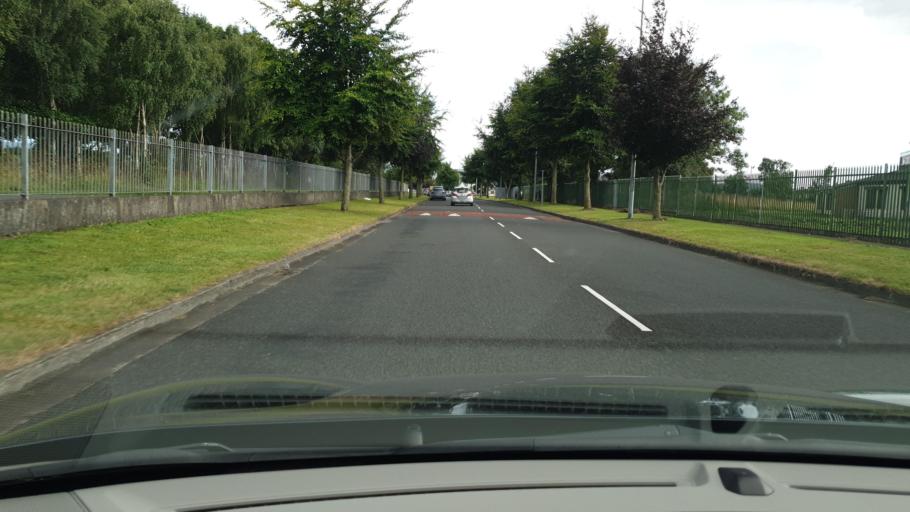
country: IE
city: Cherry Orchard
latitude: 53.3417
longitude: -6.3942
